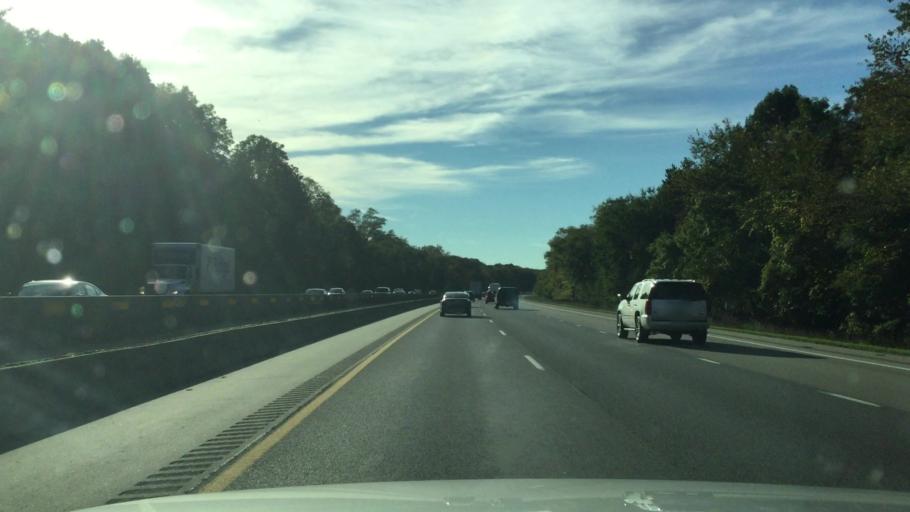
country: US
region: Michigan
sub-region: Kalamazoo County
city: Galesburg
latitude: 42.2696
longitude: -85.4500
